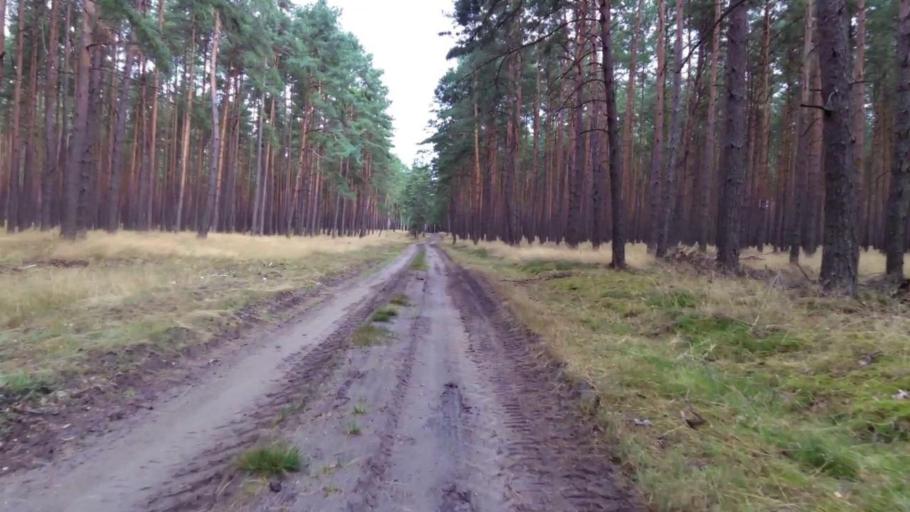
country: PL
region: West Pomeranian Voivodeship
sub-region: Powiat mysliborski
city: Debno
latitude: 52.8200
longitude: 14.6746
